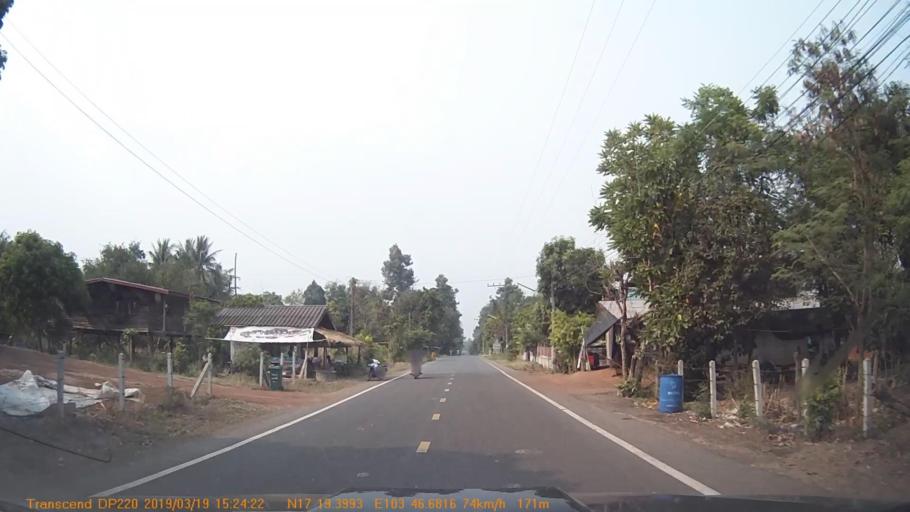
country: TH
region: Sakon Nakhon
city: Phanna Nikhom
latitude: 17.3235
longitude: 103.7780
